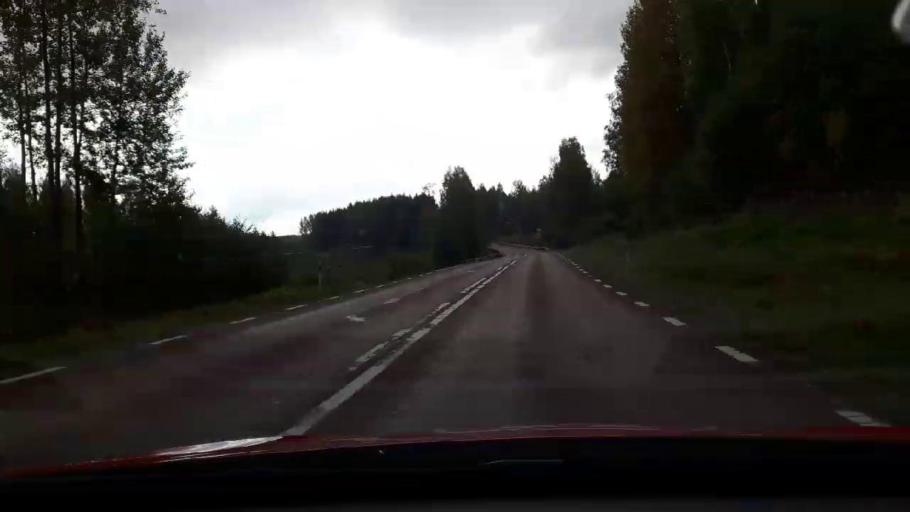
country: SE
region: Gaevleborg
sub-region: Bollnas Kommun
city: Arbra
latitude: 61.5532
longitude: 16.3490
